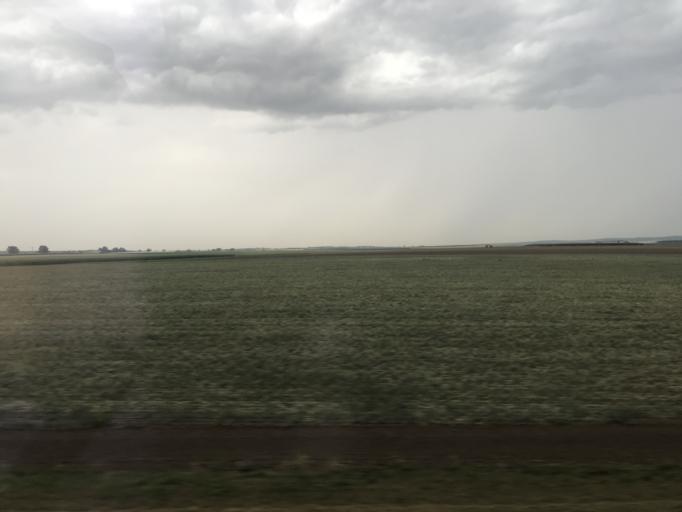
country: DE
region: Bavaria
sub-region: Regierungsbezirk Unterfranken
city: Oberpleichfeld
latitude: 49.8883
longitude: 10.0849
